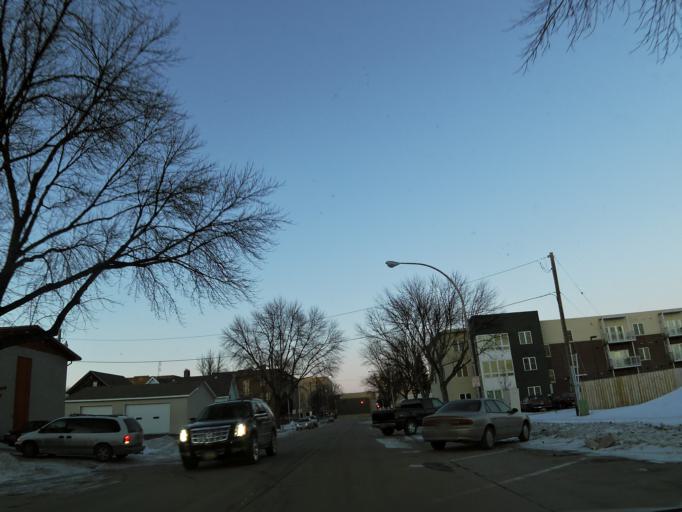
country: US
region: North Dakota
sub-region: Grand Forks County
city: Grand Forks
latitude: 47.9236
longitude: -97.0367
